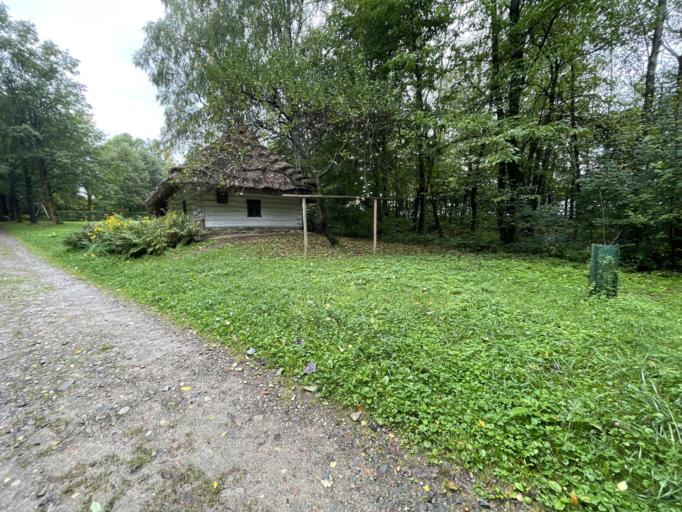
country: PL
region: Lesser Poland Voivodeship
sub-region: Powiat nowosadecki
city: Nowy Sacz
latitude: 49.6176
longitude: 20.7368
